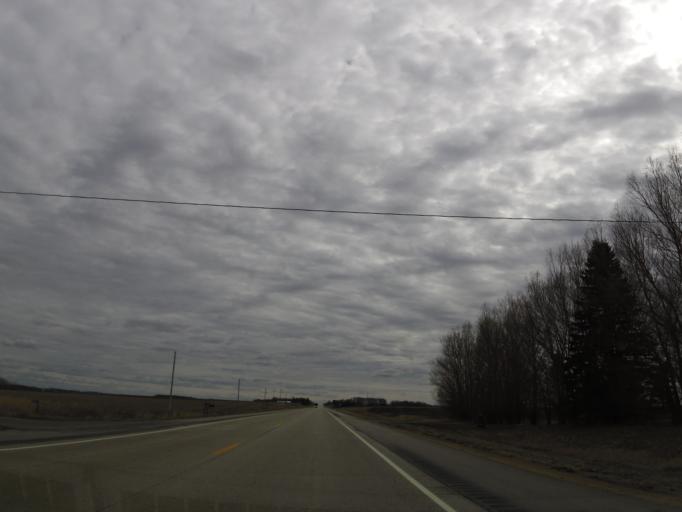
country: US
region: Minnesota
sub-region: Fillmore County
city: Spring Valley
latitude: 43.5329
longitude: -92.3694
